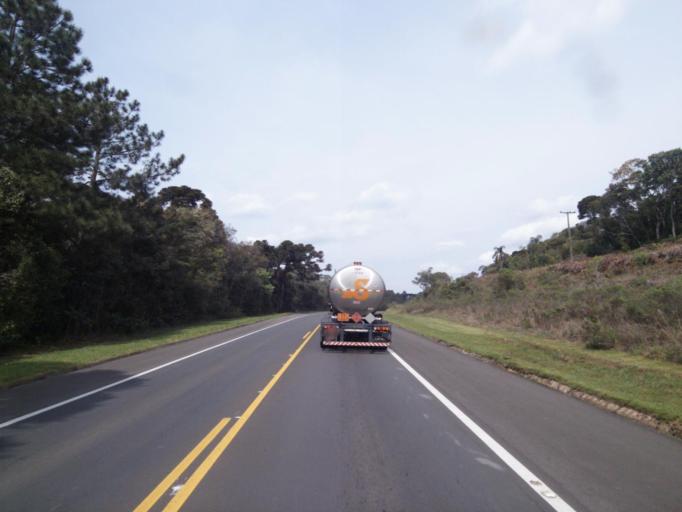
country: BR
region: Parana
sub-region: Irati
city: Irati
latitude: -25.4640
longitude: -50.4177
